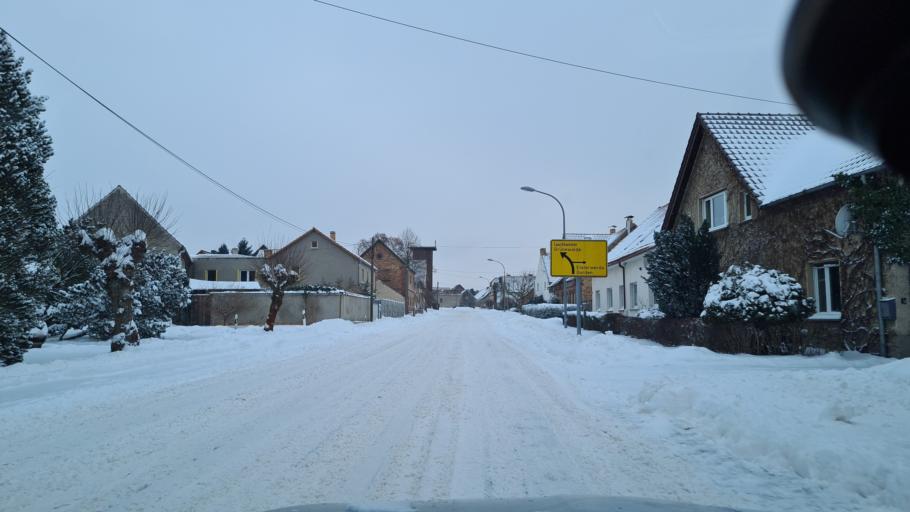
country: DE
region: Brandenburg
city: Plessa
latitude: 51.5358
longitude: 13.6655
